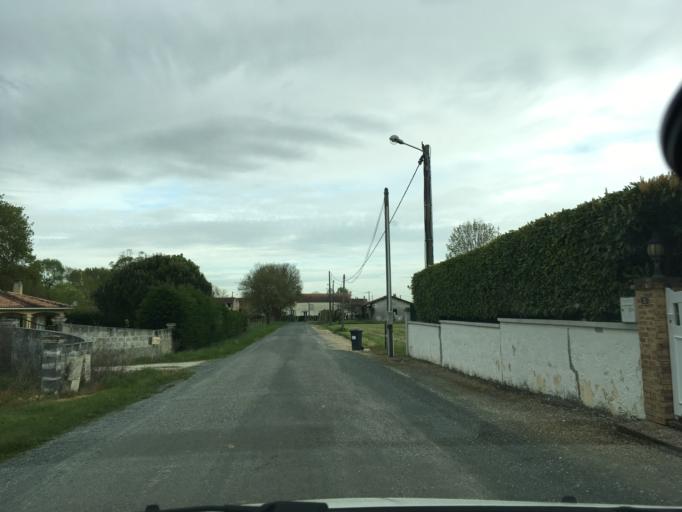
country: FR
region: Aquitaine
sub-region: Departement de la Gironde
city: Lesparre-Medoc
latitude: 45.3104
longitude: -0.8935
